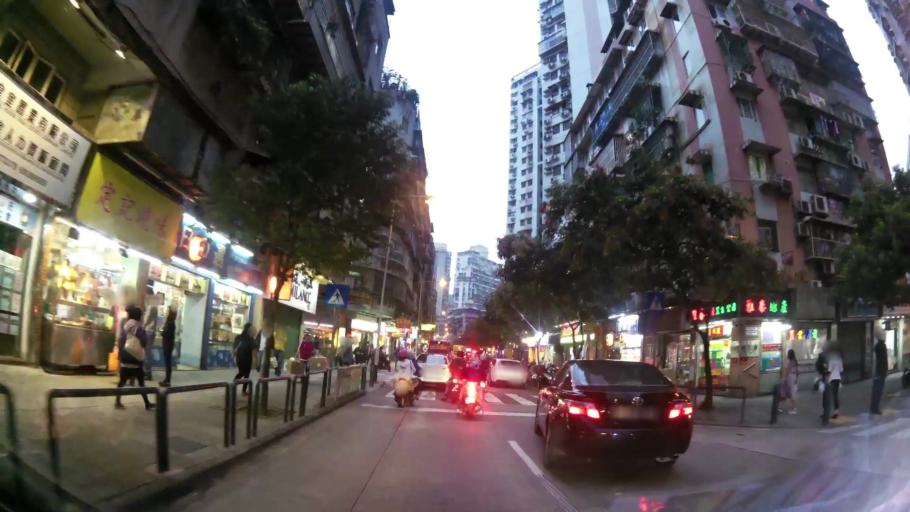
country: MO
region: Macau
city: Macau
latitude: 22.2075
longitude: 113.5500
